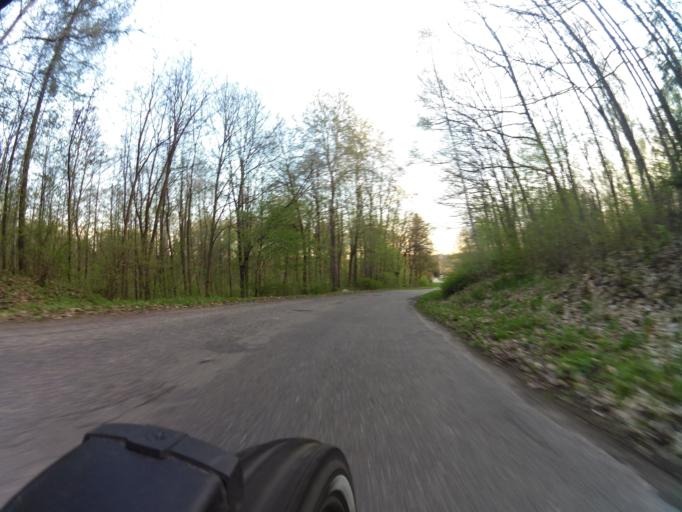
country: PL
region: West Pomeranian Voivodeship
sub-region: Powiat lobeski
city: Lobez
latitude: 53.6907
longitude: 15.6358
